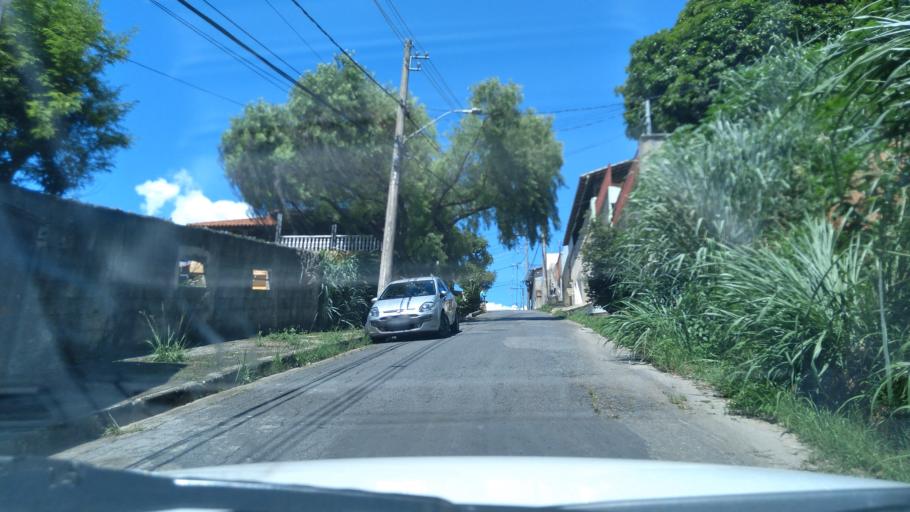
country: BR
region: Minas Gerais
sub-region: Belo Horizonte
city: Belo Horizonte
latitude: -19.8765
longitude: -43.9132
